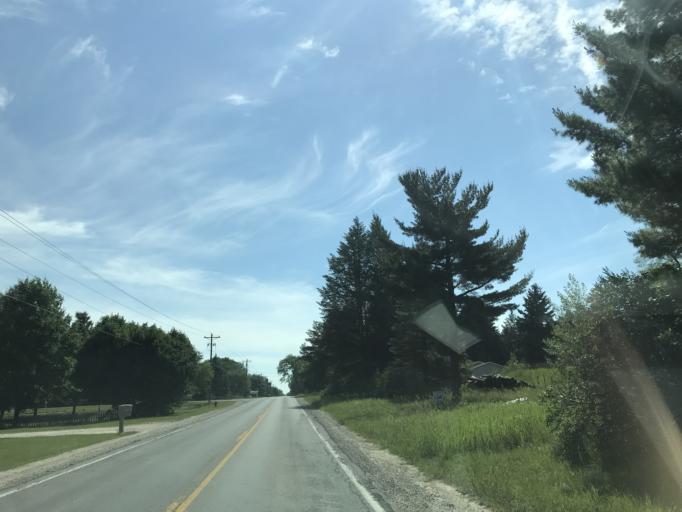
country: US
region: Michigan
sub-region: Grand Traverse County
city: Traverse City
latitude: 44.6576
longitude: -85.6853
